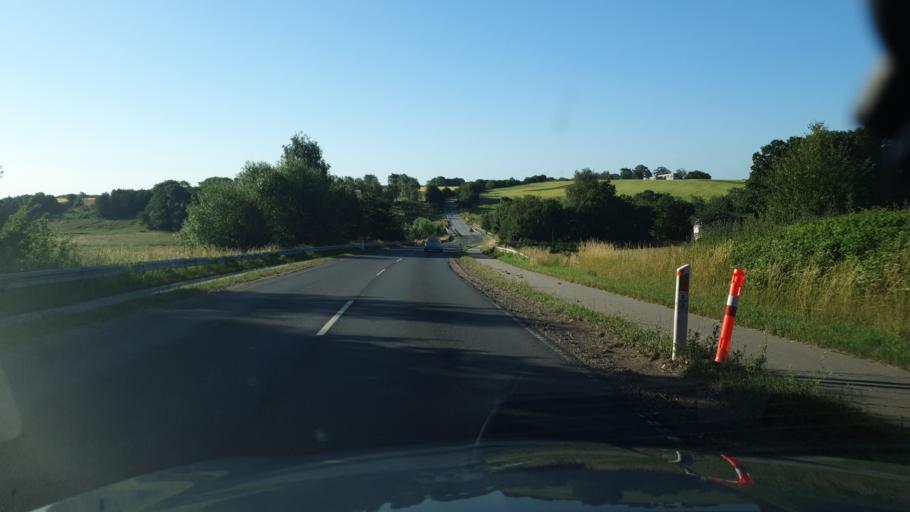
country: DK
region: Zealand
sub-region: Soro Kommune
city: Frederiksberg
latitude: 55.3886
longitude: 11.6456
